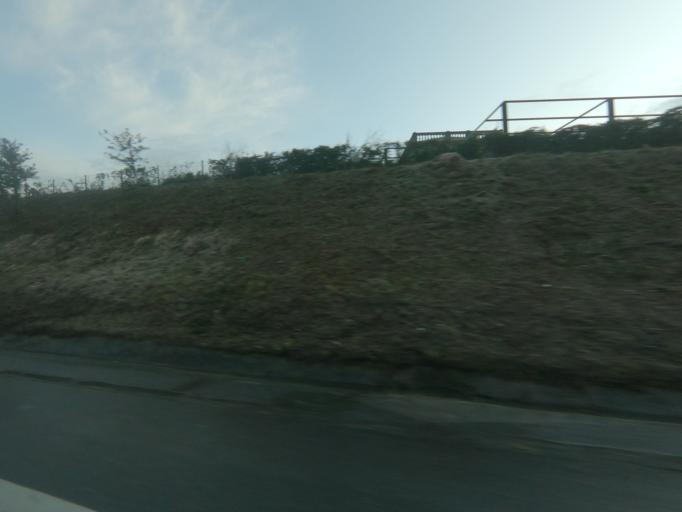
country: PT
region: Viana do Castelo
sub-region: Valenca
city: Valenca
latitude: 42.0238
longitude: -8.6495
